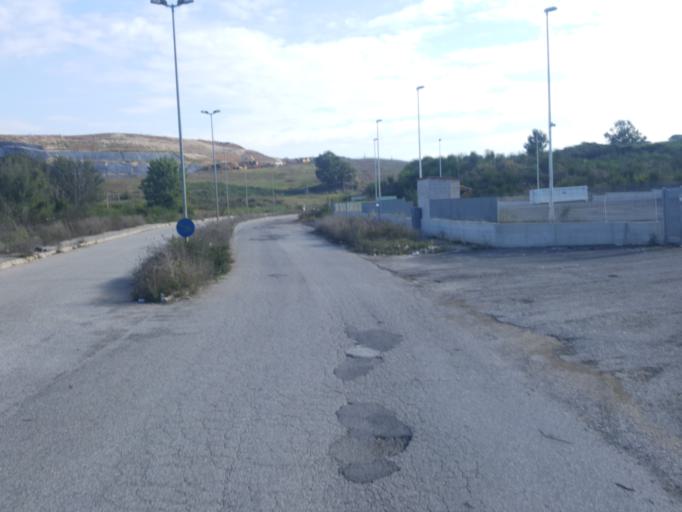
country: IT
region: Latium
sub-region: Citta metropolitana di Roma Capitale
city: Colleferro
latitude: 41.7568
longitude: 12.9977
